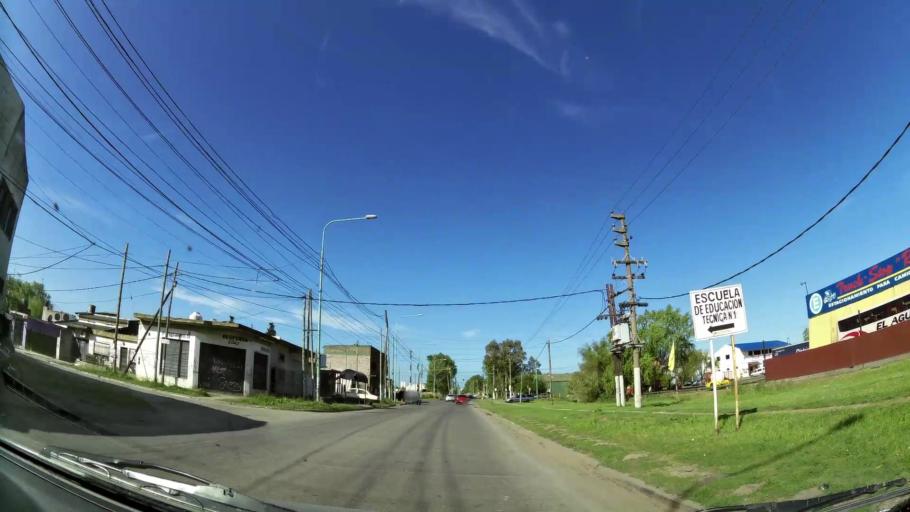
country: AR
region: Buenos Aires
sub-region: Partido de Quilmes
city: Quilmes
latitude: -34.7940
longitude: -58.2259
